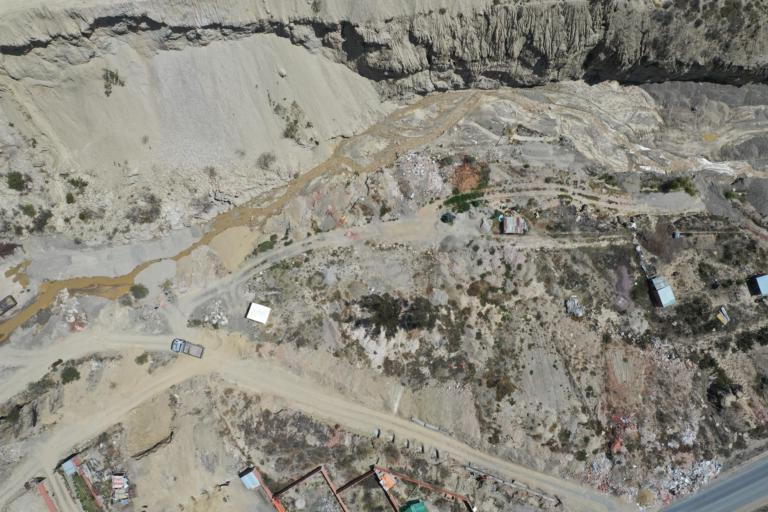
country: BO
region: La Paz
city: La Paz
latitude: -16.5638
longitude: -68.1138
